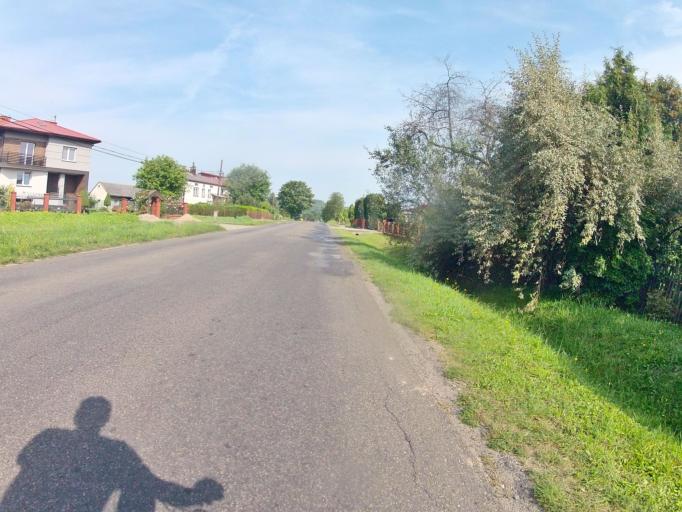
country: PL
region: Subcarpathian Voivodeship
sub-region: Powiat jasielski
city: Brzyska
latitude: 49.7867
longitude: 21.4021
